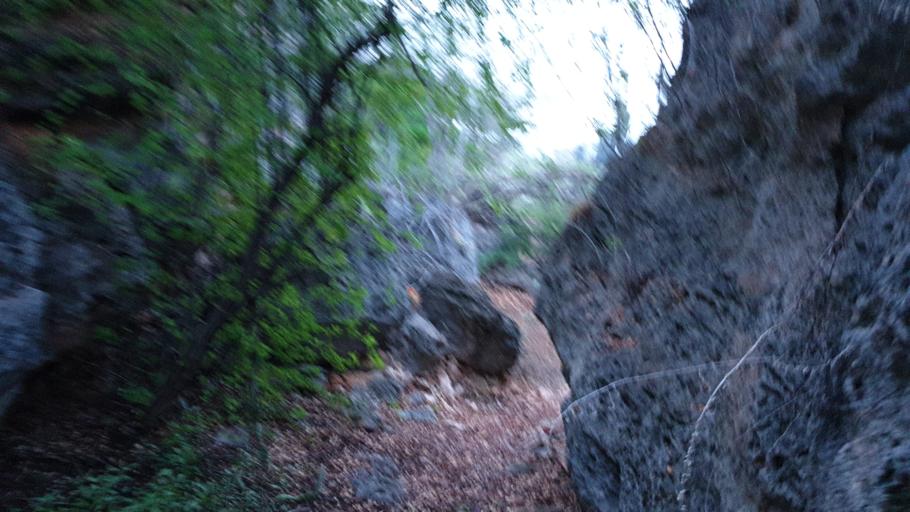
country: CW
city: Newport
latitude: 12.1321
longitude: -68.8157
